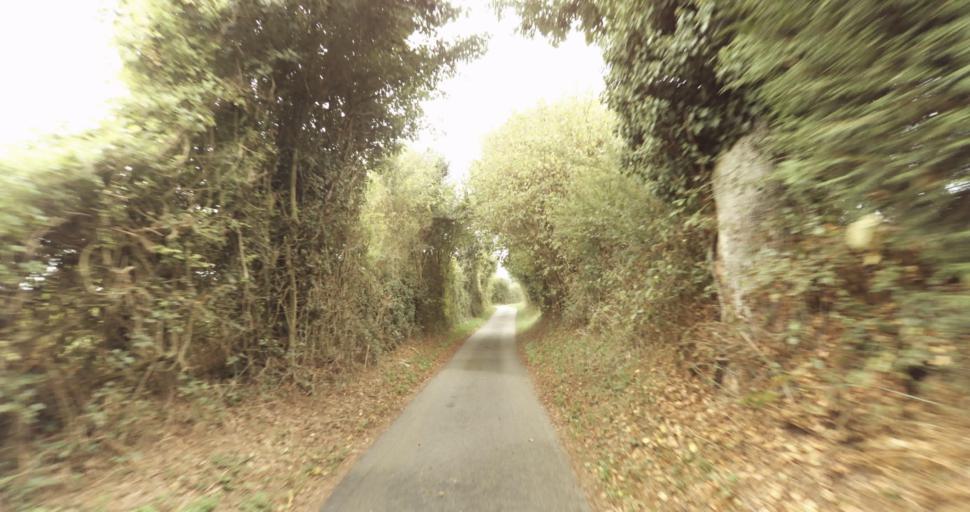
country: FR
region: Lower Normandy
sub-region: Departement de l'Orne
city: Sainte-Gauburge-Sainte-Colombe
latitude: 48.7298
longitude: 0.3580
